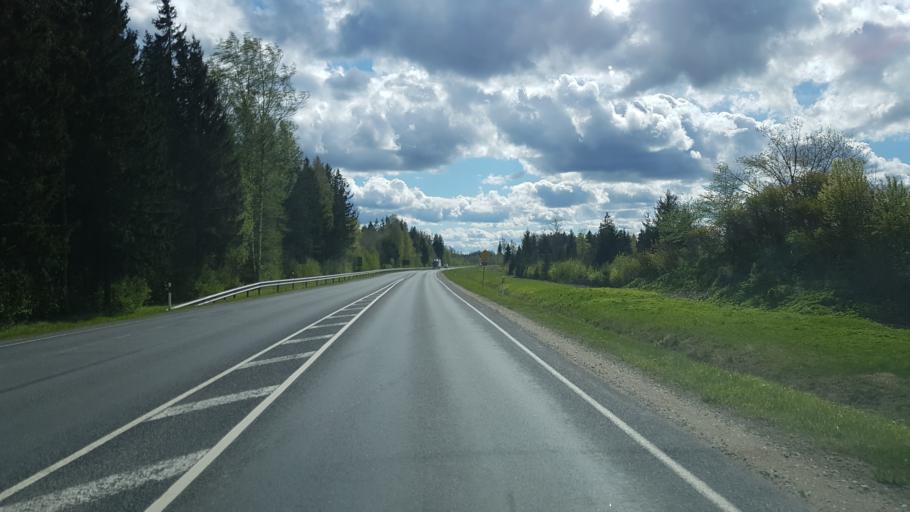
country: EE
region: Paernumaa
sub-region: Vaendra vald (alev)
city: Vandra
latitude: 58.6521
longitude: 24.9971
